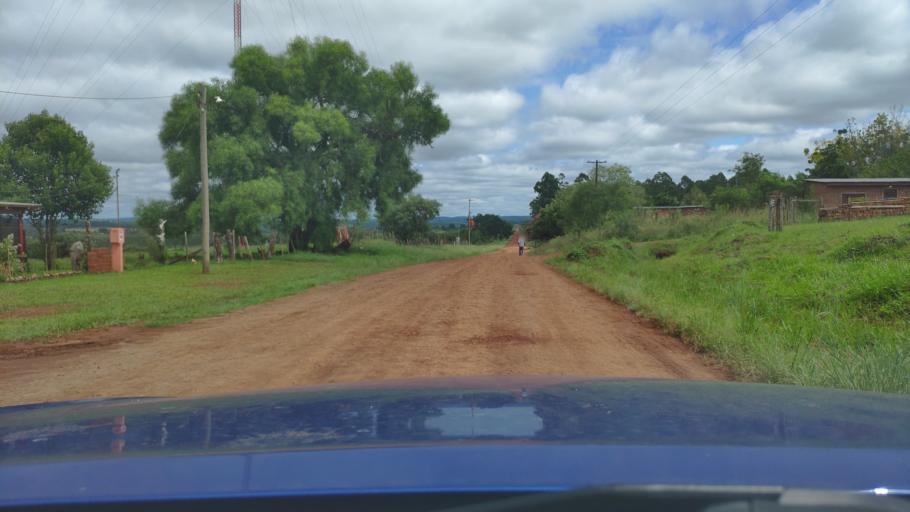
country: AR
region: Misiones
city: Santa Maria
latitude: -27.8946
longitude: -55.3565
